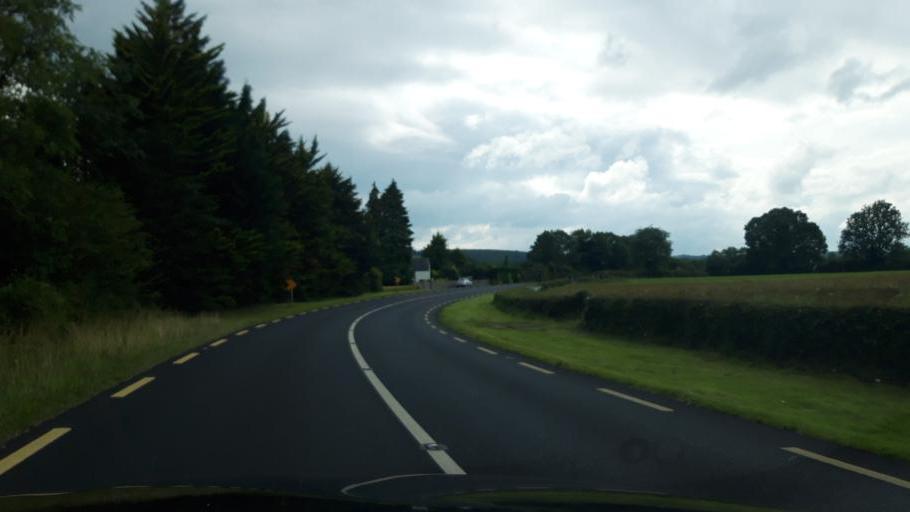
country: IE
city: Ballylinan
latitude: 52.9103
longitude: -7.0788
